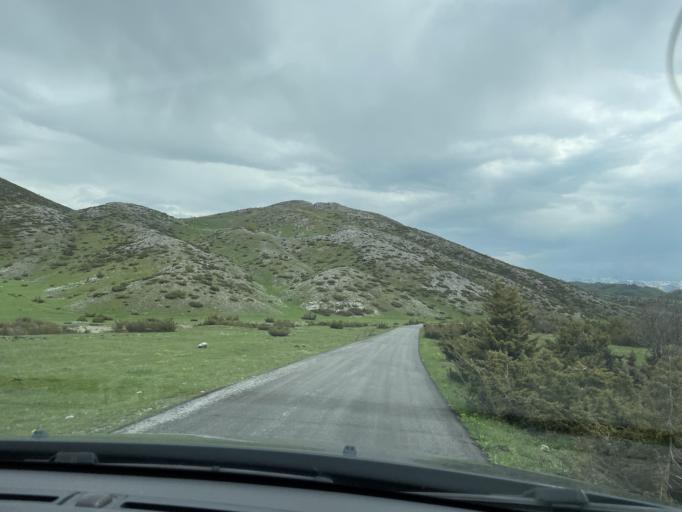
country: MK
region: Opstina Rostusa
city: Rostusha
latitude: 41.6219
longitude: 20.6853
